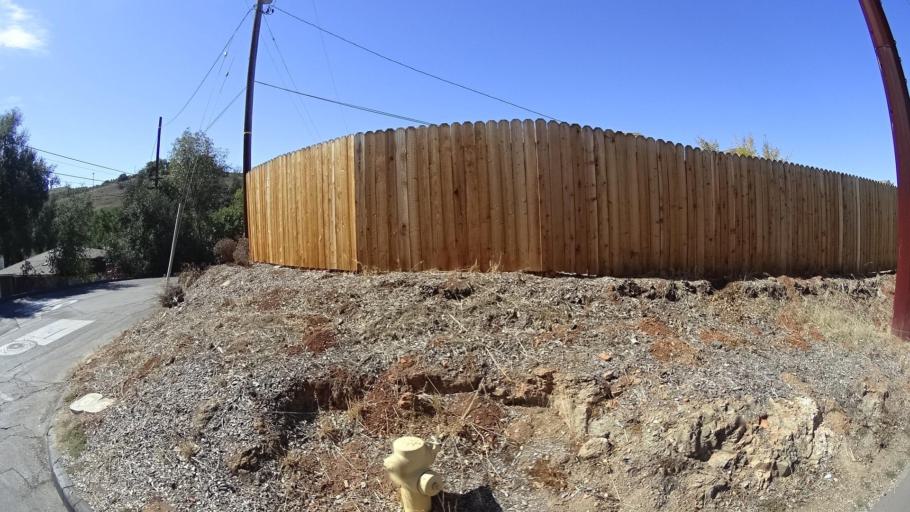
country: US
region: California
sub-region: San Diego County
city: Crest
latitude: 32.8408
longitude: -116.8760
